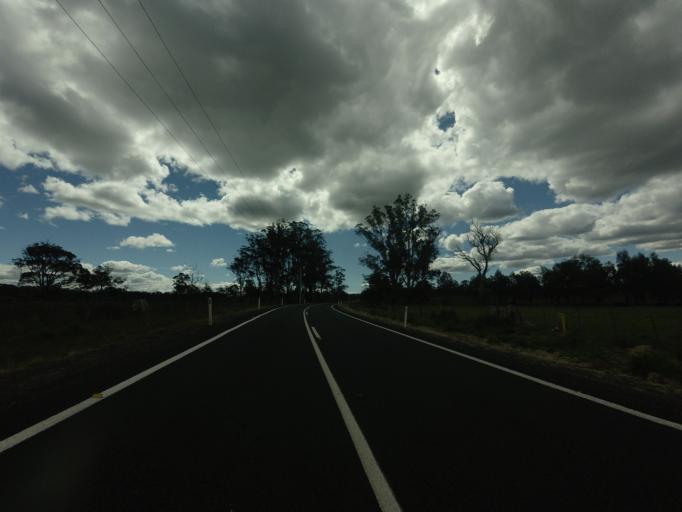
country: AU
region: Tasmania
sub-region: Northern Midlands
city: Evandale
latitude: -41.9882
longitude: 147.6735
